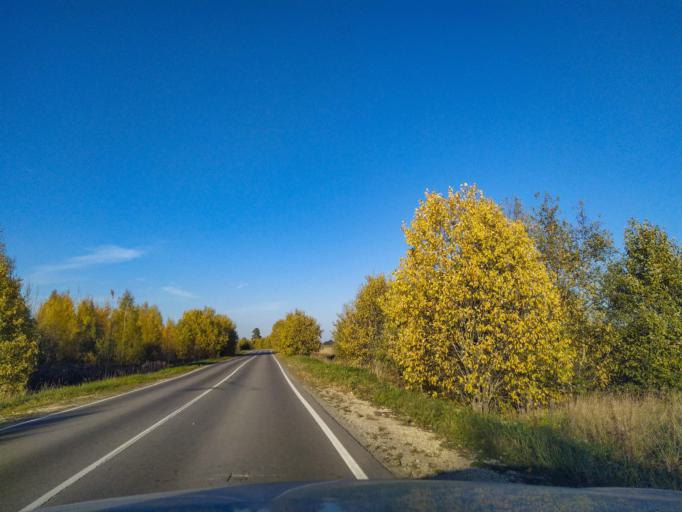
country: RU
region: Leningrad
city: Siverskiy
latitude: 59.3109
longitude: 30.0303
